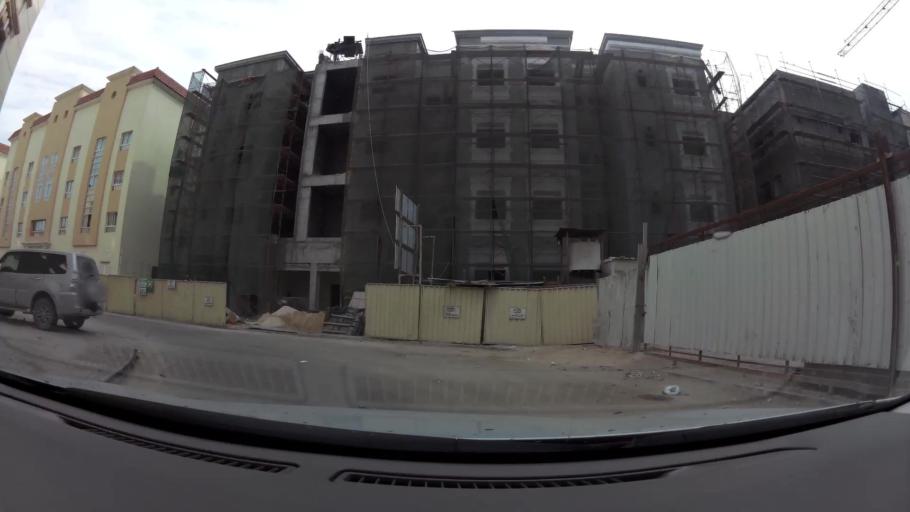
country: QA
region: Baladiyat ad Dawhah
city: Doha
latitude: 25.2763
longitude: 51.4928
